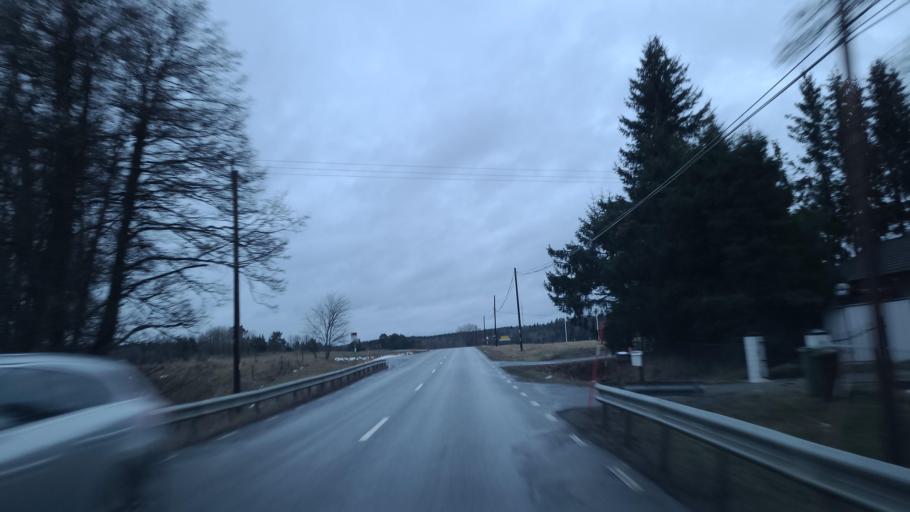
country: SE
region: Stockholm
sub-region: Osterakers Kommun
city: Akersberga
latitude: 59.6135
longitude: 18.3250
